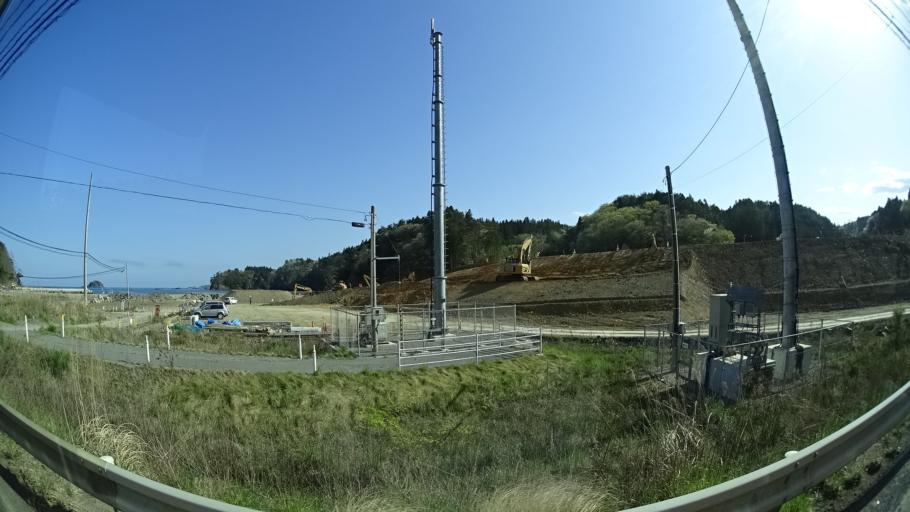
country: JP
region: Miyagi
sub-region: Oshika Gun
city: Onagawa Cho
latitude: 38.6914
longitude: 141.4902
